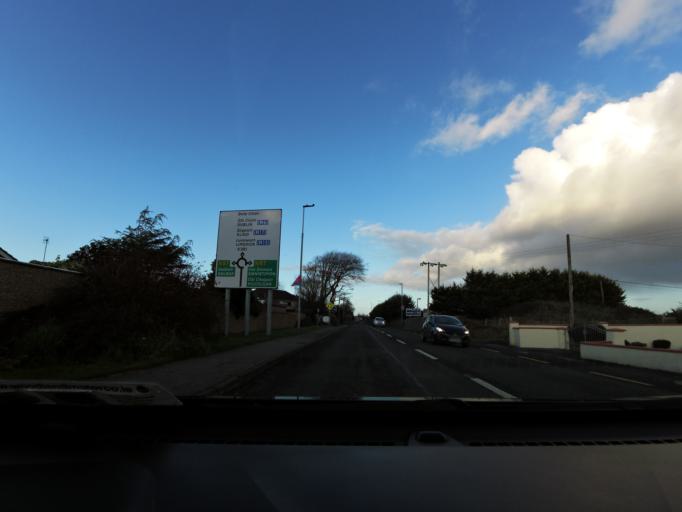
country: IE
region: Connaught
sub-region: County Galway
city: Oranmore
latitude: 53.2742
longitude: -8.9278
